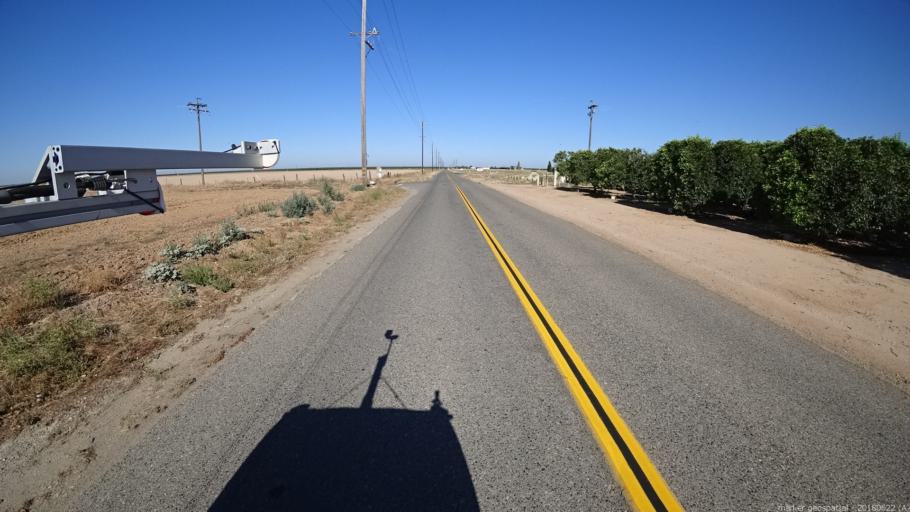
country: US
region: California
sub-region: Madera County
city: Bonadelle Ranchos-Madera Ranchos
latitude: 36.8951
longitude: -119.8105
